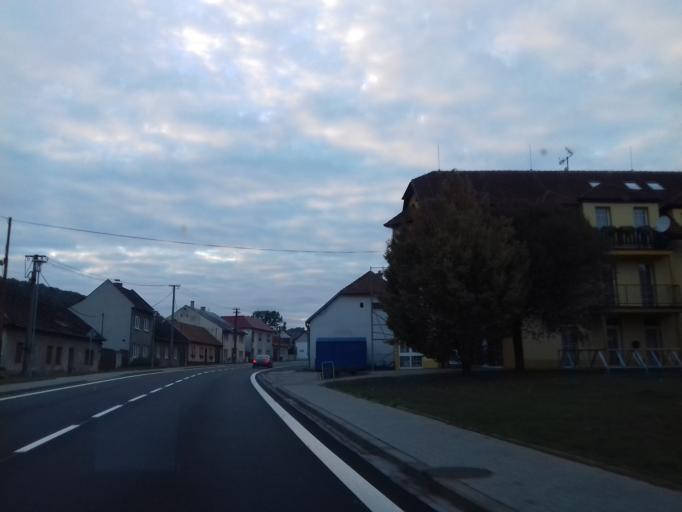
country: CZ
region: Zlin
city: Bojkovice
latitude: 48.9652
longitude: 17.8644
